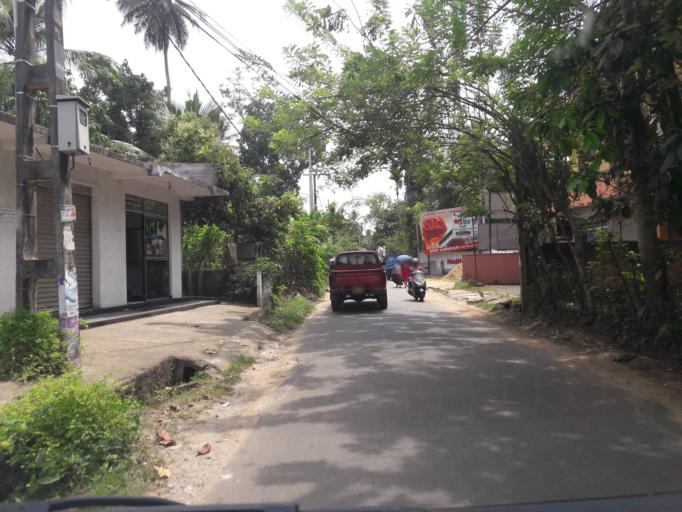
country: LK
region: Southern
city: Hikkaduwa
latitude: 6.0953
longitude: 80.1481
